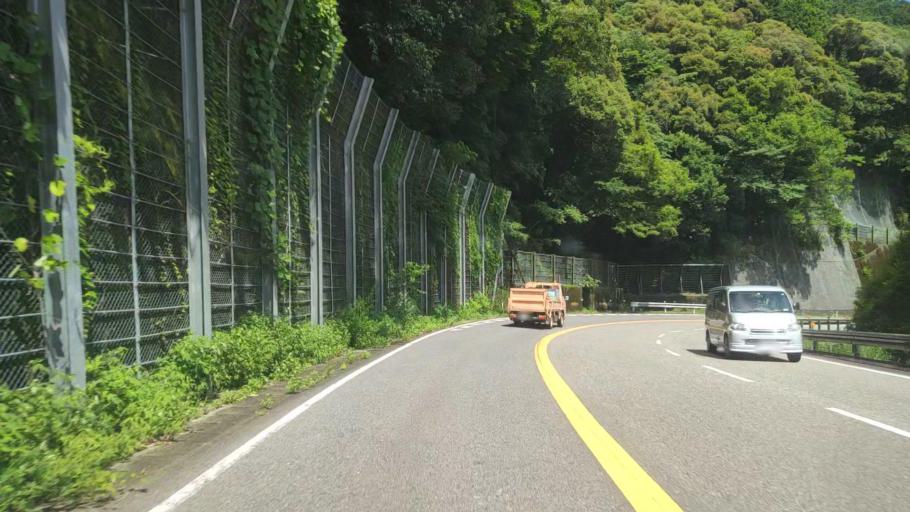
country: JP
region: Mie
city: Owase
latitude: 33.9203
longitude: 136.1022
